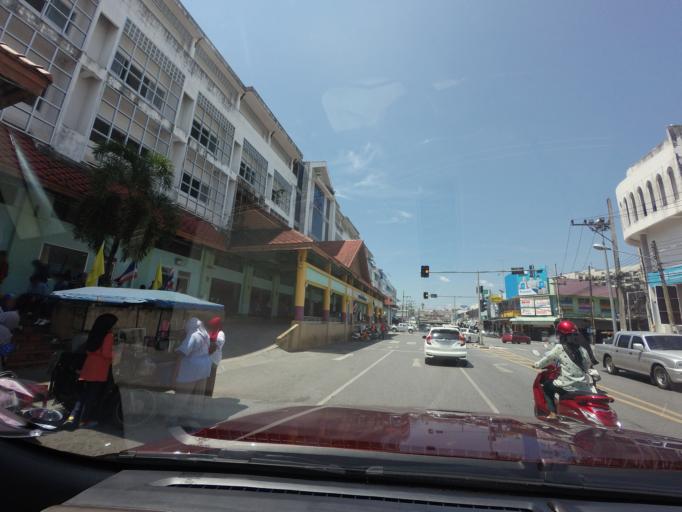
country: TH
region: Yala
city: Yala
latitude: 6.5606
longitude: 101.2925
